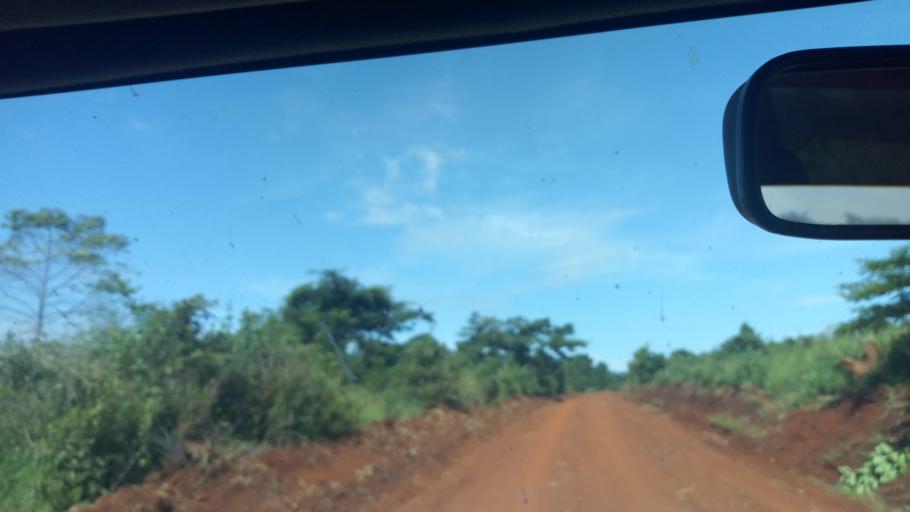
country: UG
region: Western Region
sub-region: Masindi District
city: Masindi
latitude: 1.6454
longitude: 31.7745
